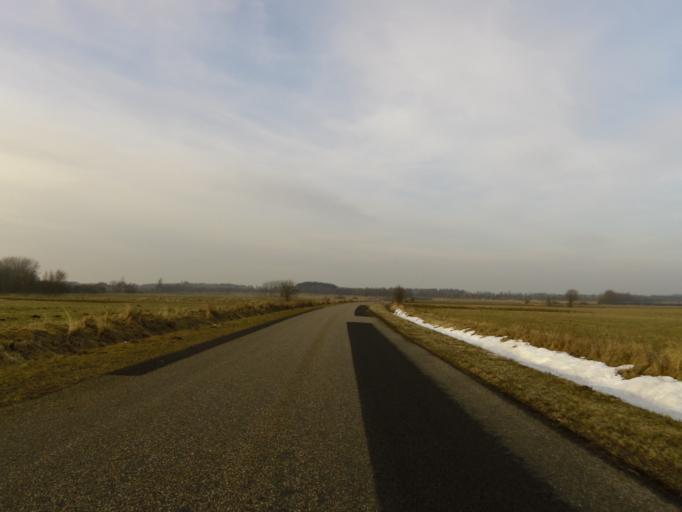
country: DK
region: South Denmark
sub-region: Tonder Kommune
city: Logumkloster
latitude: 55.1509
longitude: 8.8987
